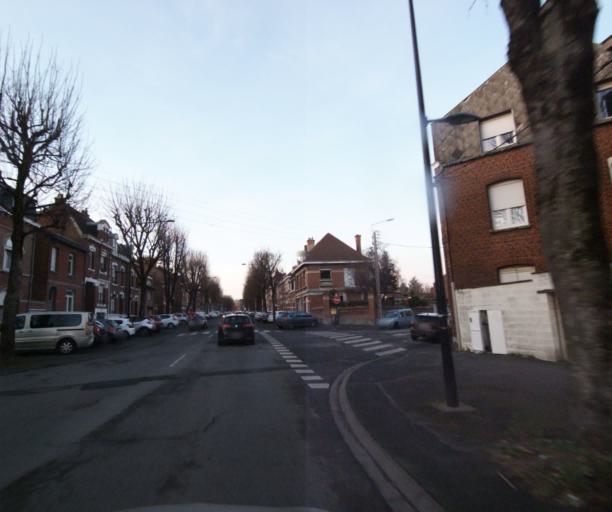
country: FR
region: Nord-Pas-de-Calais
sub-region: Departement du Nord
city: Anzin
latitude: 50.3611
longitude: 3.5112
